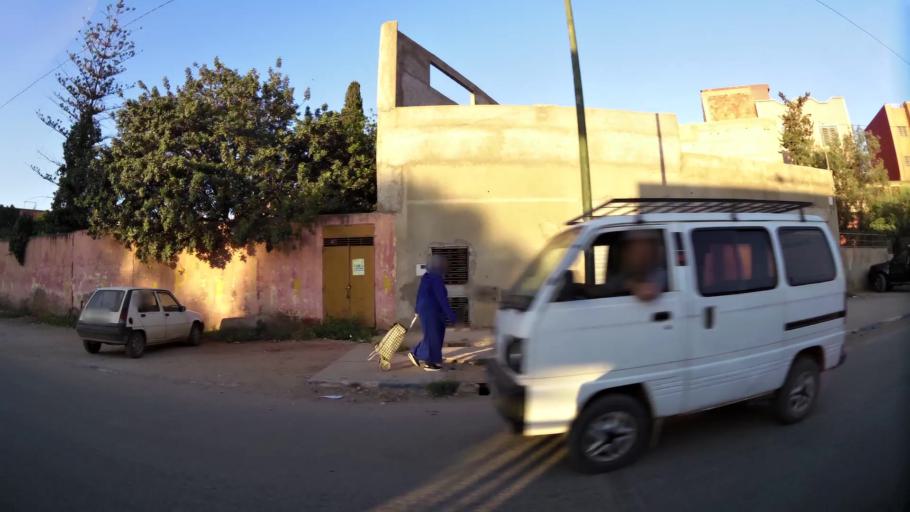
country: MA
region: Oriental
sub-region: Berkane-Taourirt
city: Berkane
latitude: 34.9205
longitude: -2.3299
